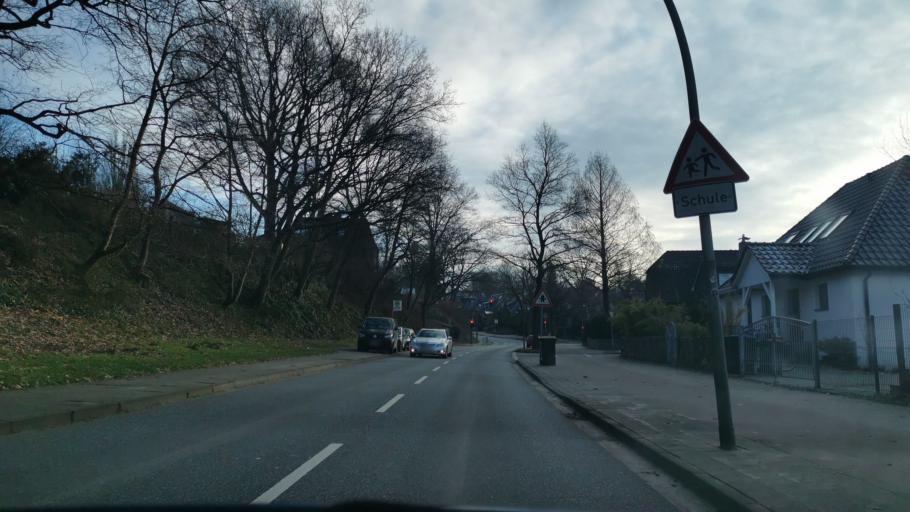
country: DE
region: Hamburg
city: Harburg
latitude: 53.4349
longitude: 9.9688
